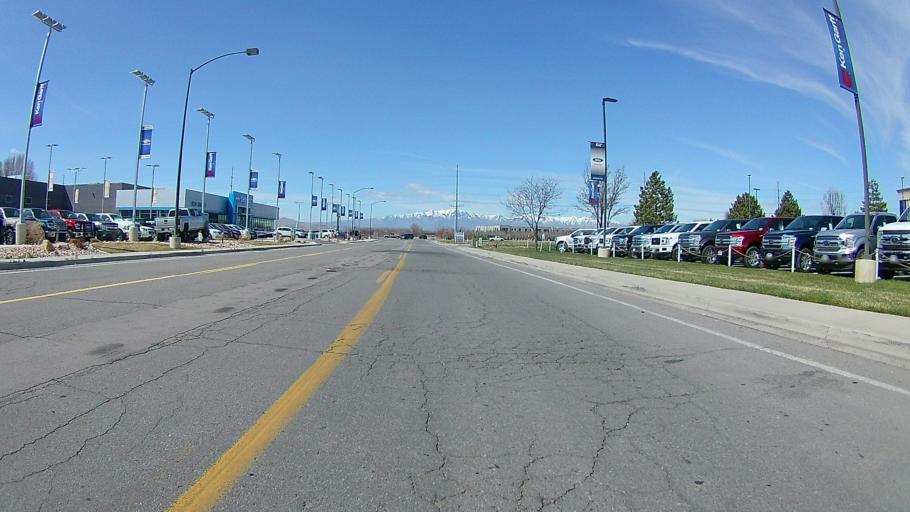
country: US
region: Utah
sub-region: Utah County
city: American Fork
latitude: 40.3572
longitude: -111.7835
